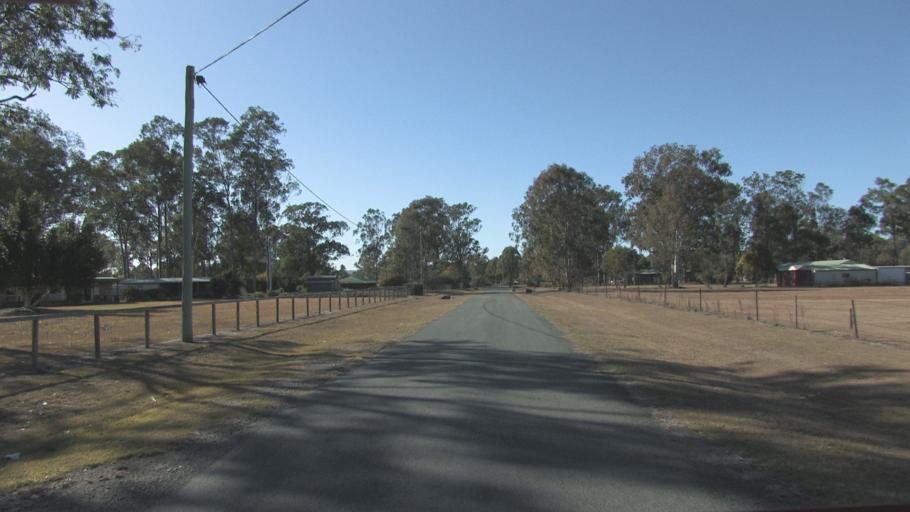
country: AU
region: Queensland
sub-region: Logan
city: North Maclean
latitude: -27.8297
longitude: 152.9904
